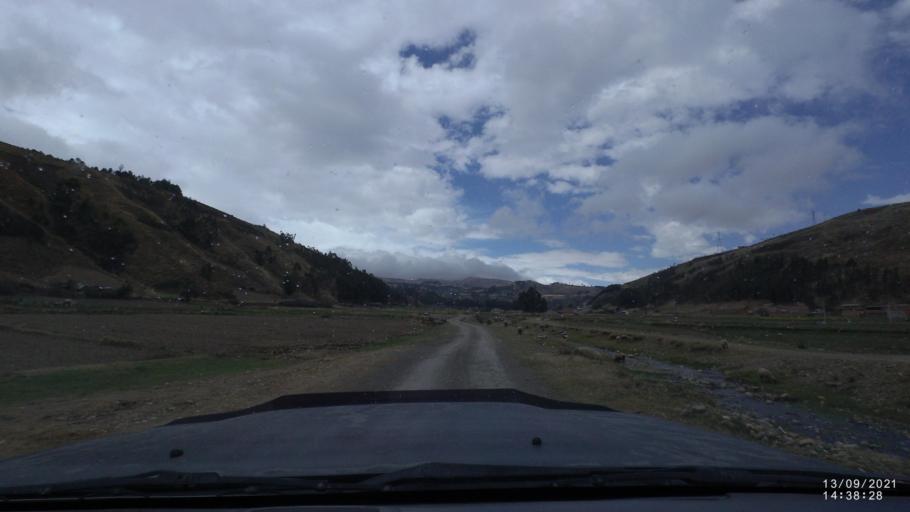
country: BO
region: Cochabamba
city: Colomi
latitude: -17.3698
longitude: -65.8318
